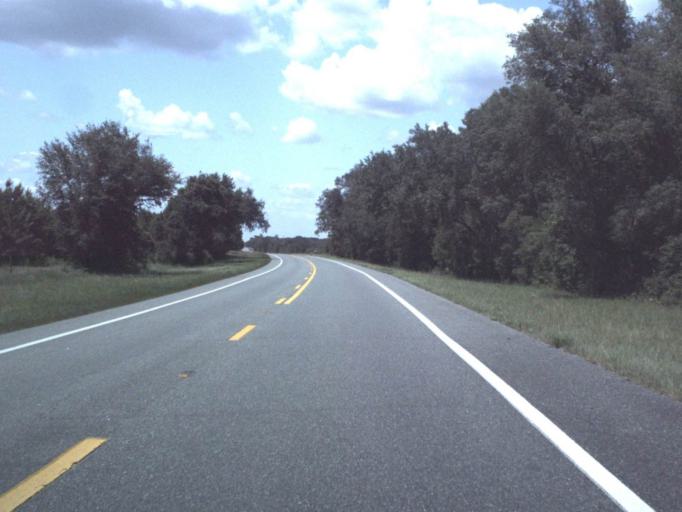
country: US
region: Florida
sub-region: Gilchrist County
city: Trenton
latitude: 29.7401
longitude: -82.7406
